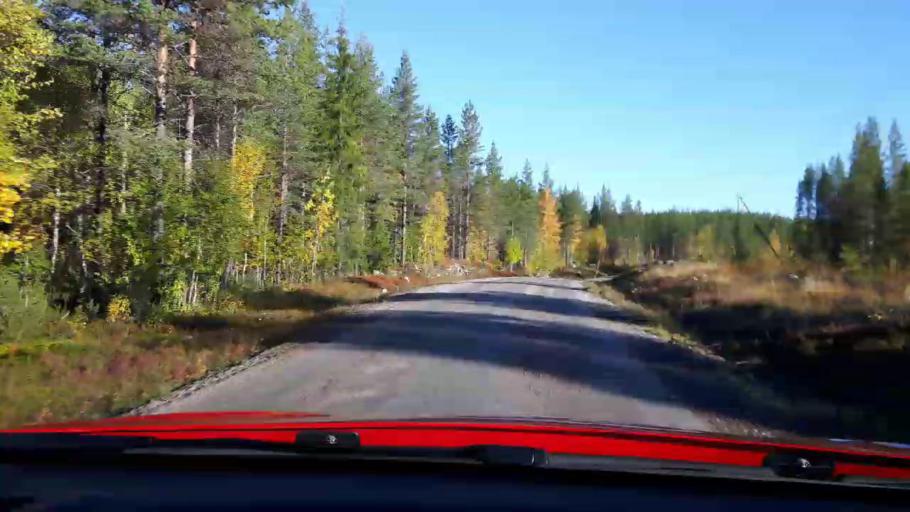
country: SE
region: Jaemtland
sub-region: Stroemsunds Kommun
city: Stroemsund
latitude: 64.3796
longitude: 15.1487
